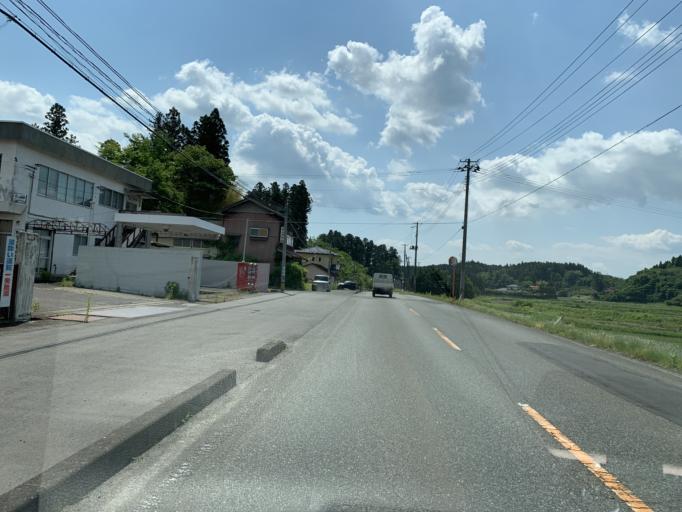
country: JP
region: Miyagi
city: Furukawa
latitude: 38.6956
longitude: 140.9289
